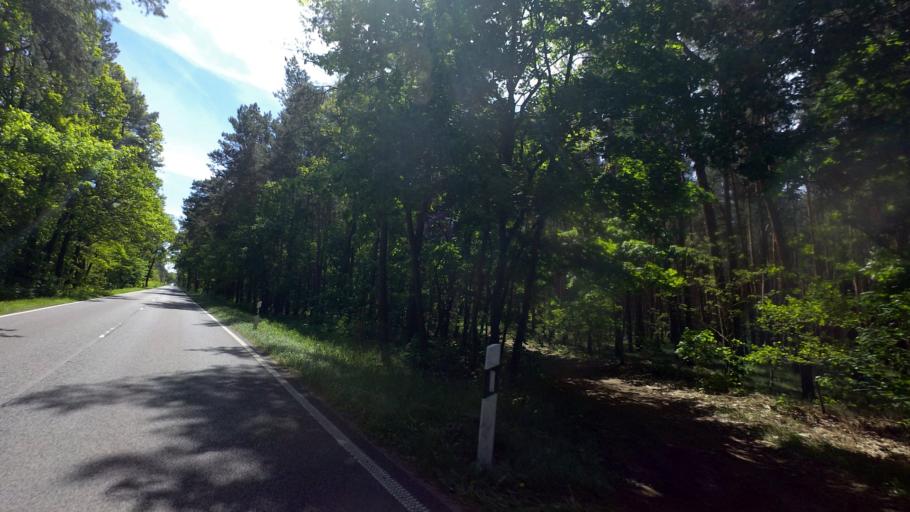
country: DE
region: Brandenburg
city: Luckenwalde
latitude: 52.1569
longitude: 13.1032
